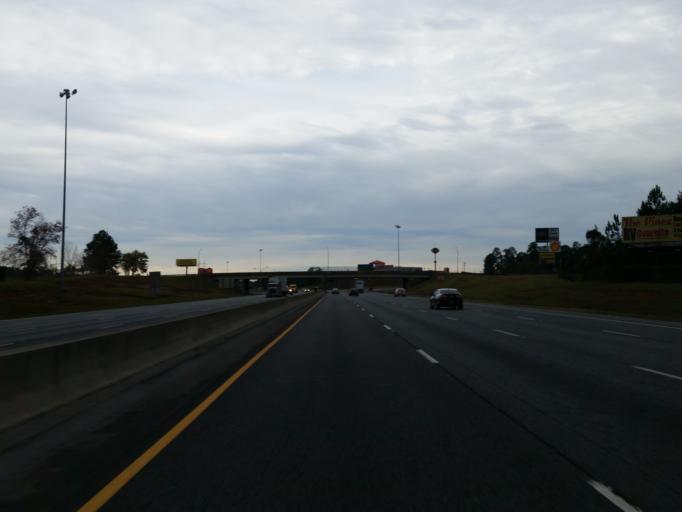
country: US
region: Georgia
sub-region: Tift County
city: Tifton
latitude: 31.4442
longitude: -83.5288
